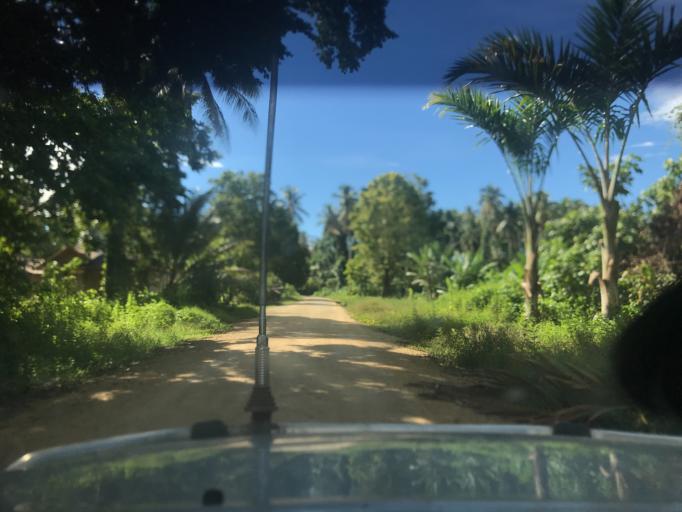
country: SB
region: Malaita
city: Auki
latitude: -8.3704
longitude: 160.6722
